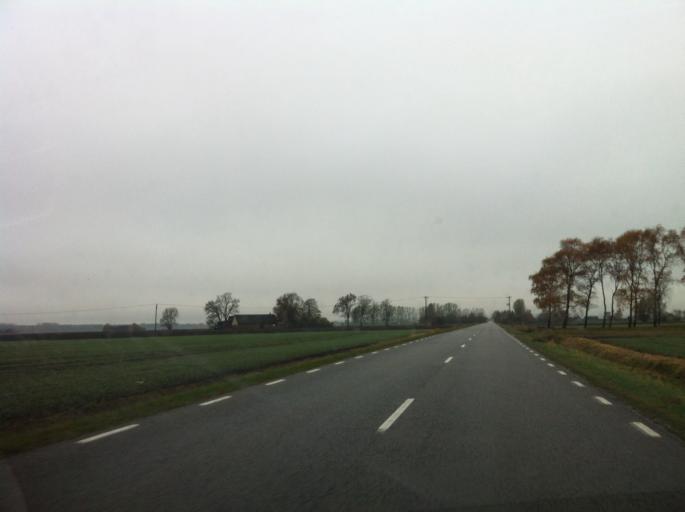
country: SE
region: Skane
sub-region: Landskrona
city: Asmundtorp
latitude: 55.8627
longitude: 12.9984
